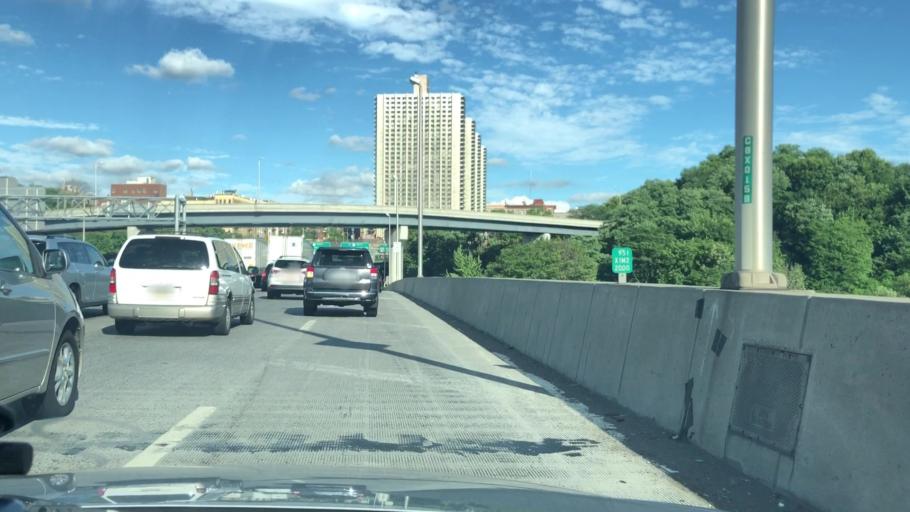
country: US
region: New York
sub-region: New York County
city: Inwood
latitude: 40.8456
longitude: -73.9283
